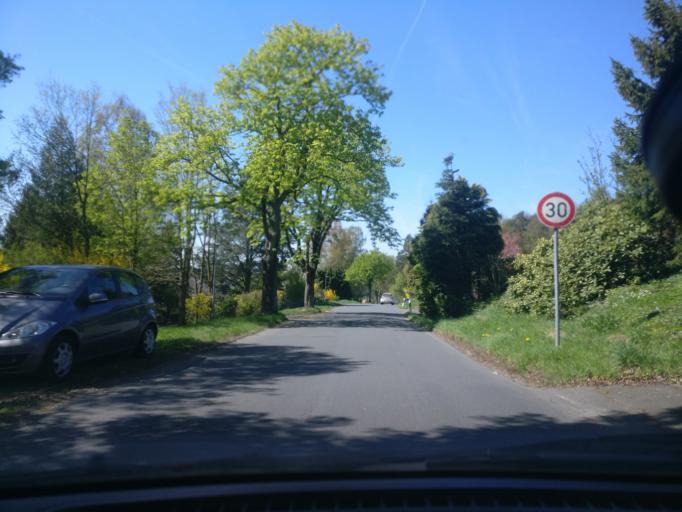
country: DE
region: Lower Saxony
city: Hannoversch Munden
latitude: 51.4060
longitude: 9.6674
